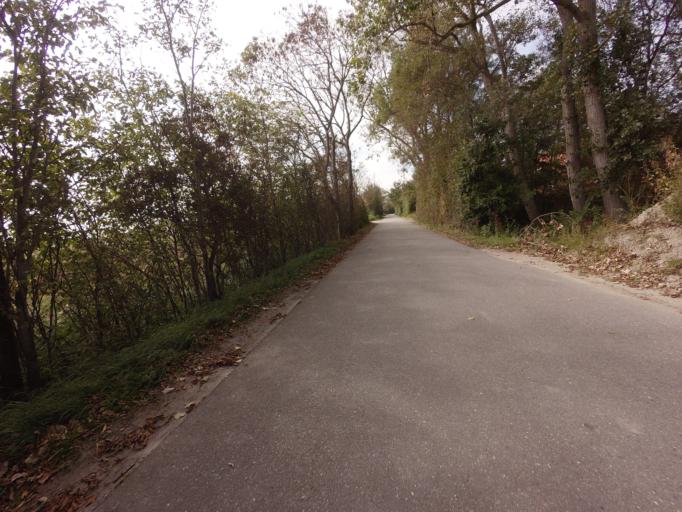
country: NL
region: Zeeland
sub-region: Gemeente Vlissingen
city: Vlissingen
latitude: 51.5209
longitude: 3.4713
